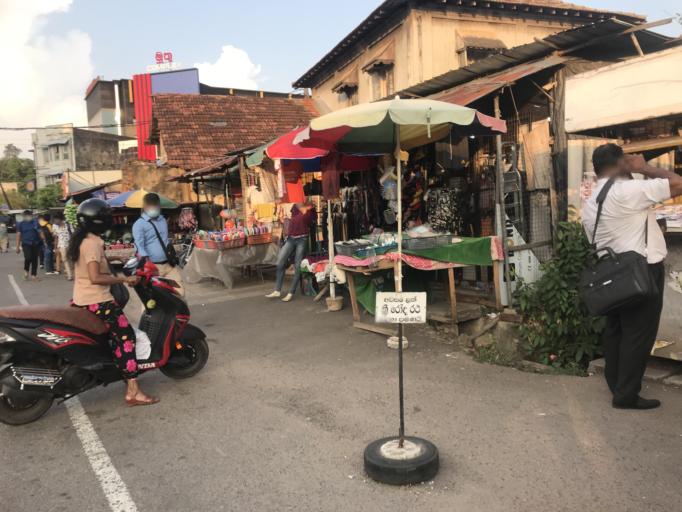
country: LK
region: Western
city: Gampaha
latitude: 7.0927
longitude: 79.9935
